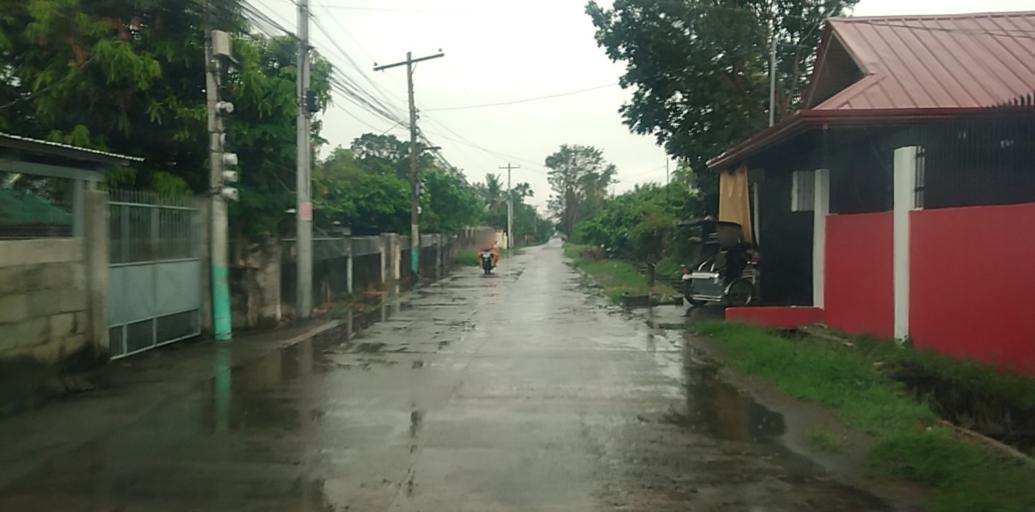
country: PH
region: Central Luzon
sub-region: Province of Pampanga
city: Arenas
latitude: 15.1667
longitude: 120.6882
